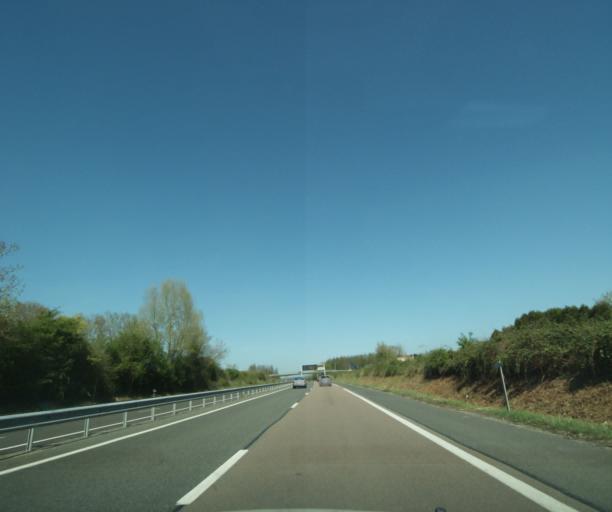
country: FR
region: Bourgogne
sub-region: Departement de la Nievre
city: Cosne-Cours-sur-Loire
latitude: 47.3944
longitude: 2.9329
